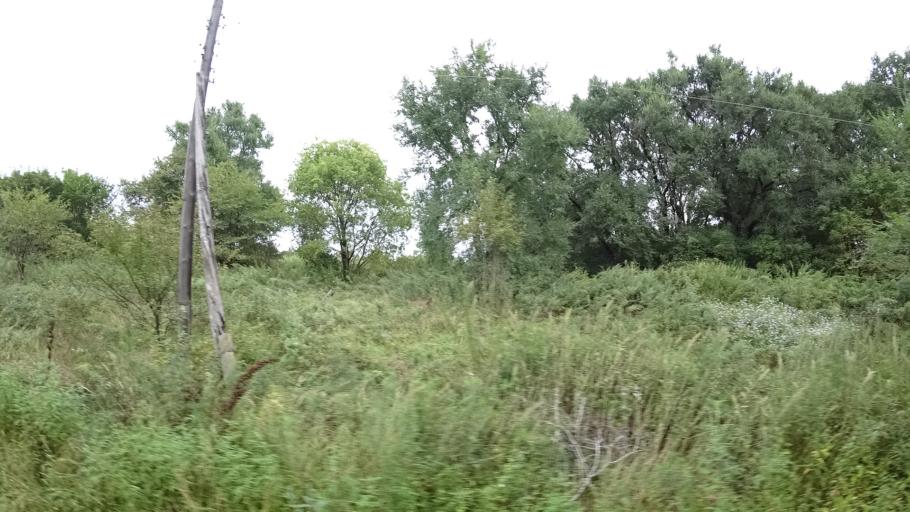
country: RU
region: Primorskiy
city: Rettikhovka
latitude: 44.1314
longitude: 132.6345
